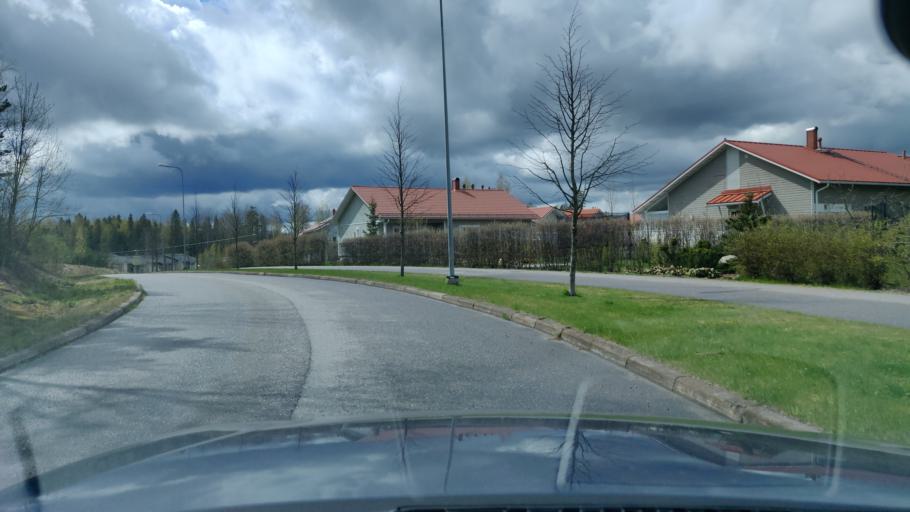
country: FI
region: Uusimaa
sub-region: Helsinki
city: Nurmijaervi
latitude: 60.3639
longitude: 24.7289
